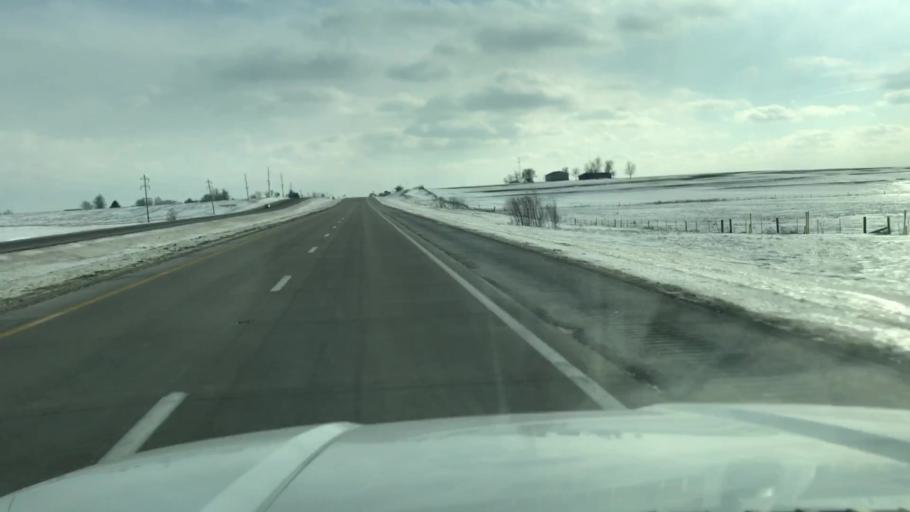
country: US
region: Missouri
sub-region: Nodaway County
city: Maryville
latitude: 40.2650
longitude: -94.8670
